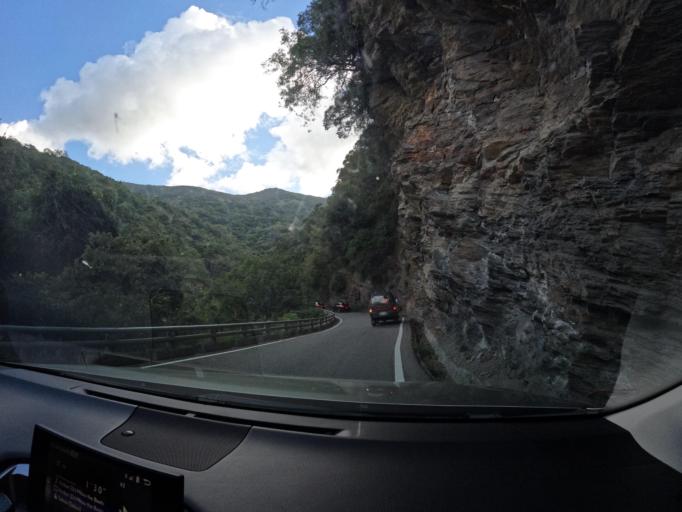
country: TW
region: Taiwan
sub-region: Taitung
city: Taitung
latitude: 23.1607
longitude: 121.0502
